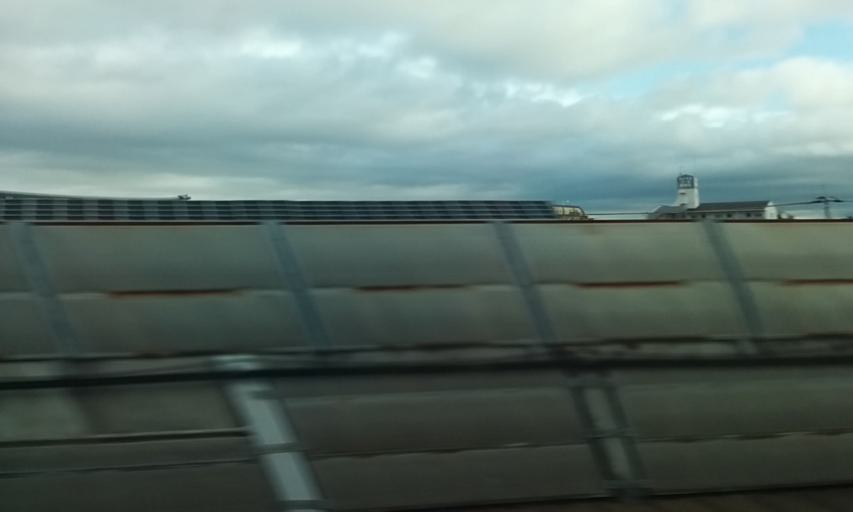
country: JP
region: Hyogo
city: Akashi
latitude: 34.6663
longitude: 134.9687
